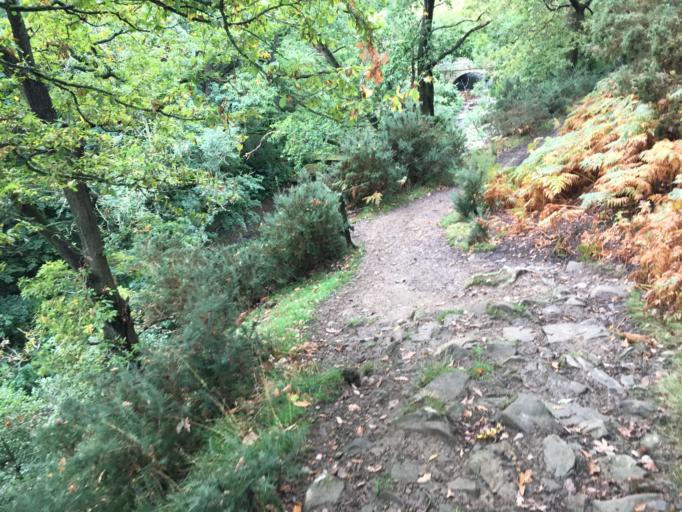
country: GB
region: England
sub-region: North Yorkshire
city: Sleights
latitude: 54.4094
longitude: -0.7343
